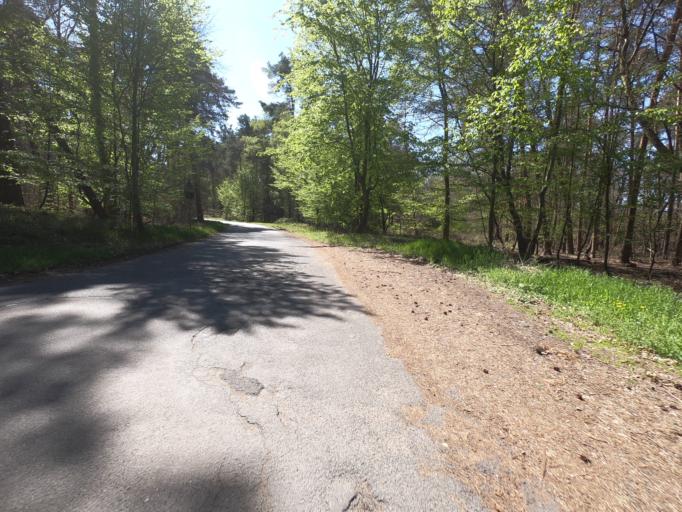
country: DE
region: Hesse
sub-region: Regierungsbezirk Darmstadt
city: Erzhausen
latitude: 49.9437
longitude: 8.6130
